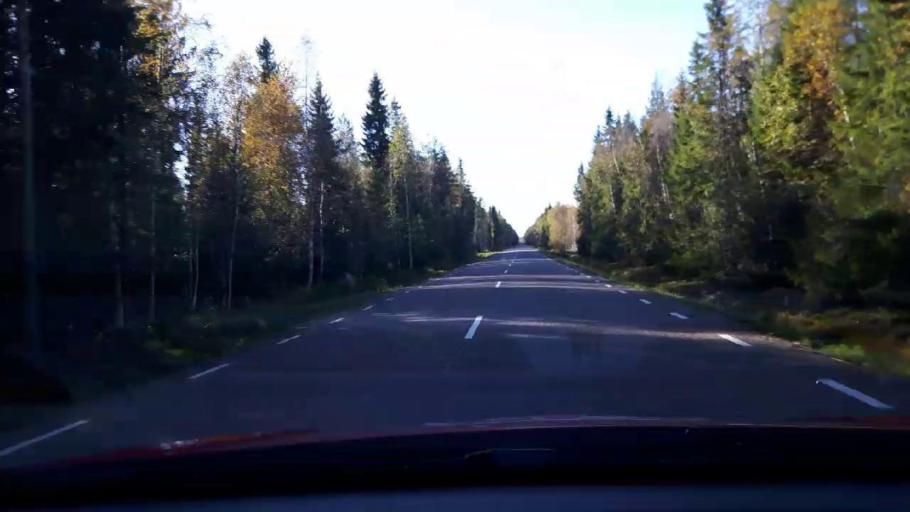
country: SE
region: Jaemtland
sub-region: Stroemsunds Kommun
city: Stroemsund
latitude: 63.8508
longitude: 15.2558
